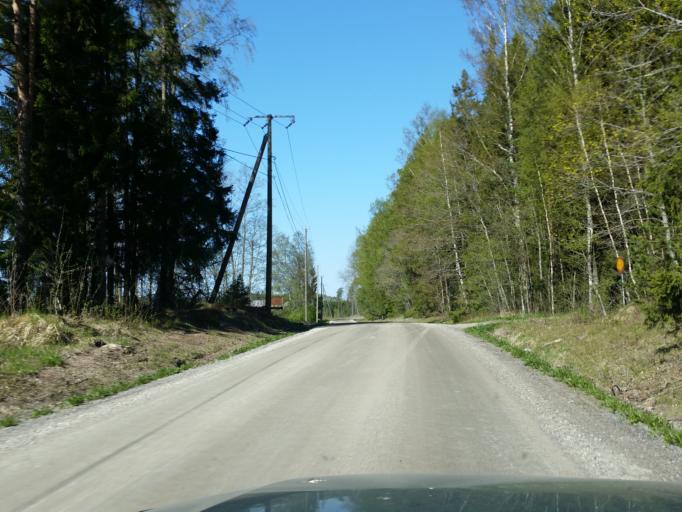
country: FI
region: Uusimaa
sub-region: Helsinki
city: Karjalohja
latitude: 60.1439
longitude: 23.8165
